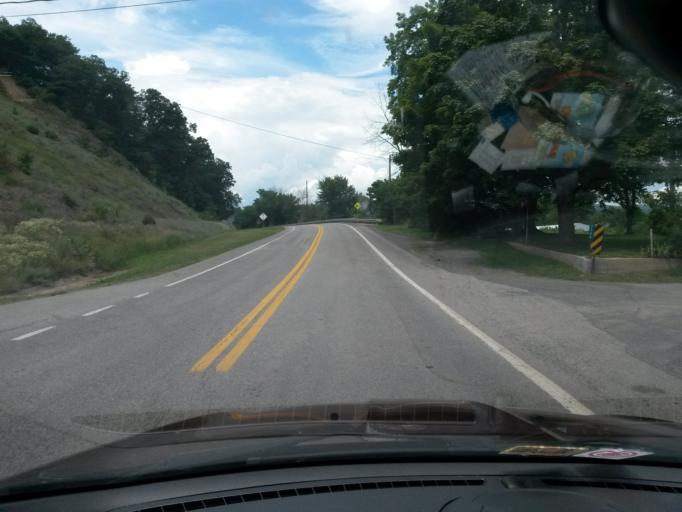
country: US
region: West Virginia
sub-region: Grant County
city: Petersburg
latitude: 38.9929
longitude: -79.0451
